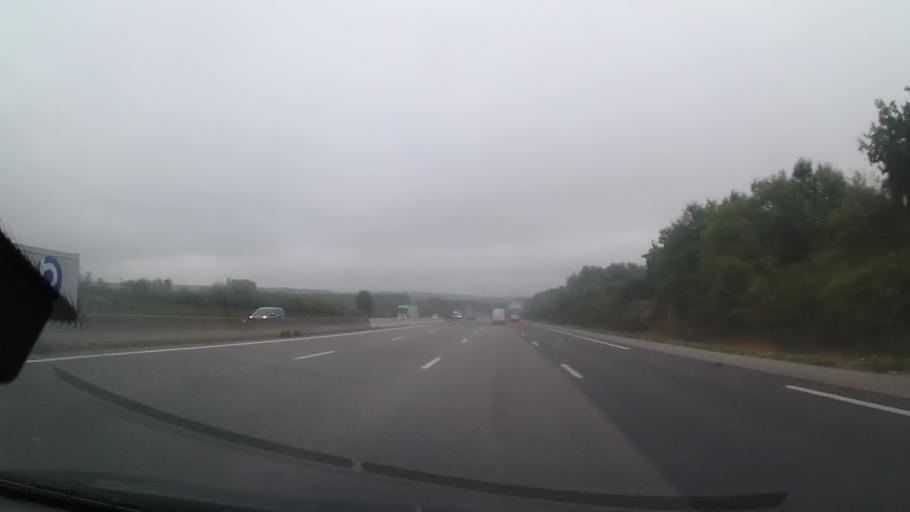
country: FR
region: Ile-de-France
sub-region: Departement de l'Essonne
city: Vaugrigneuse
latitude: 48.6107
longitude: 2.1068
